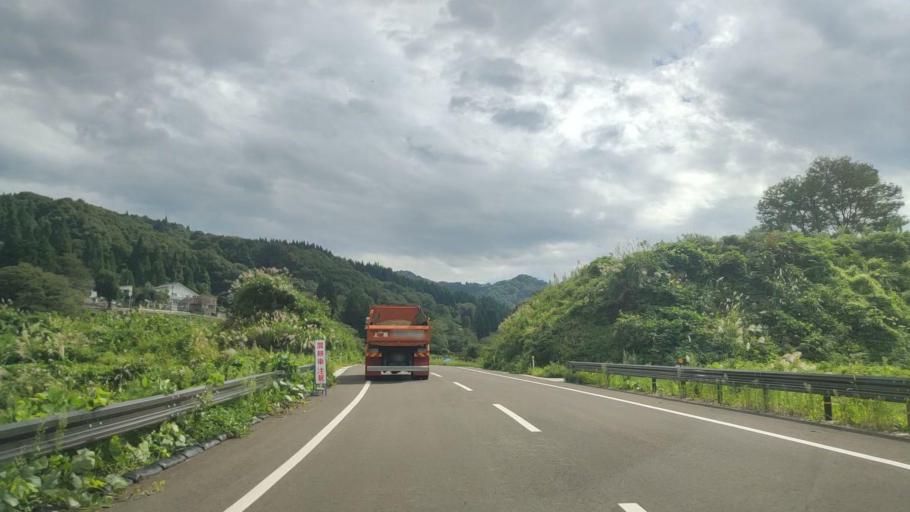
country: JP
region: Niigata
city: Arai
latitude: 36.9491
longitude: 138.2822
